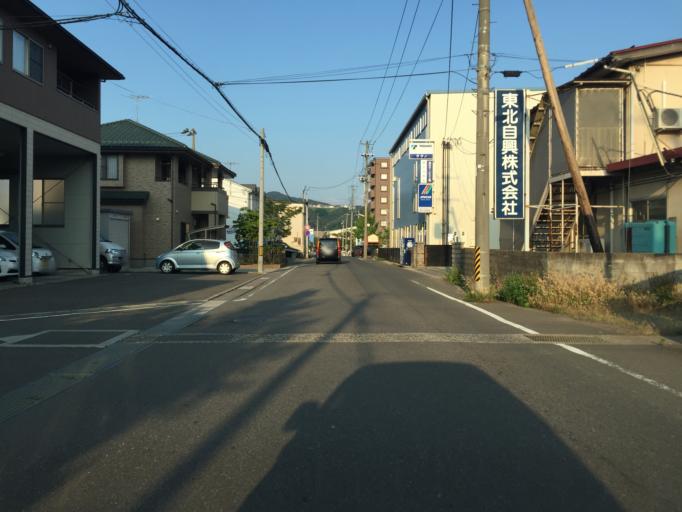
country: JP
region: Fukushima
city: Fukushima-shi
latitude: 37.7294
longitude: 140.4623
